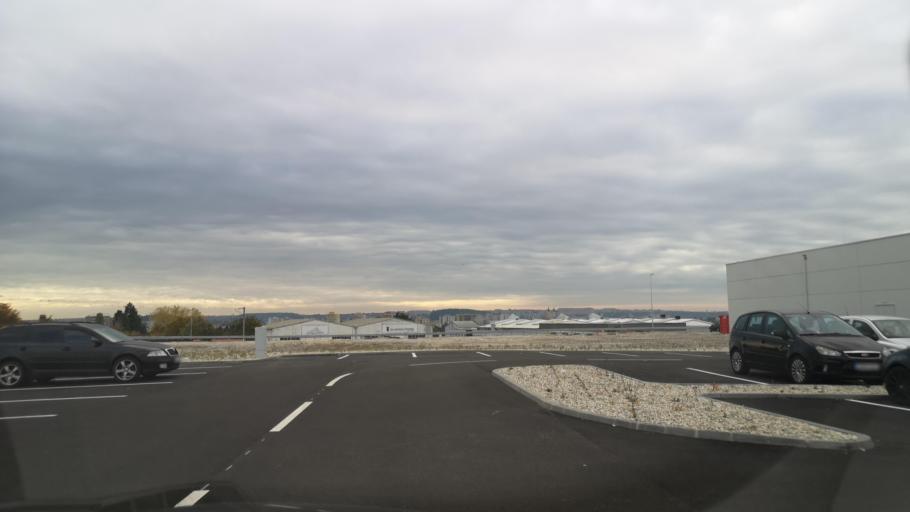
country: SK
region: Nitriansky
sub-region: Okres Nitra
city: Nitra
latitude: 48.3185
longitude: 18.1166
